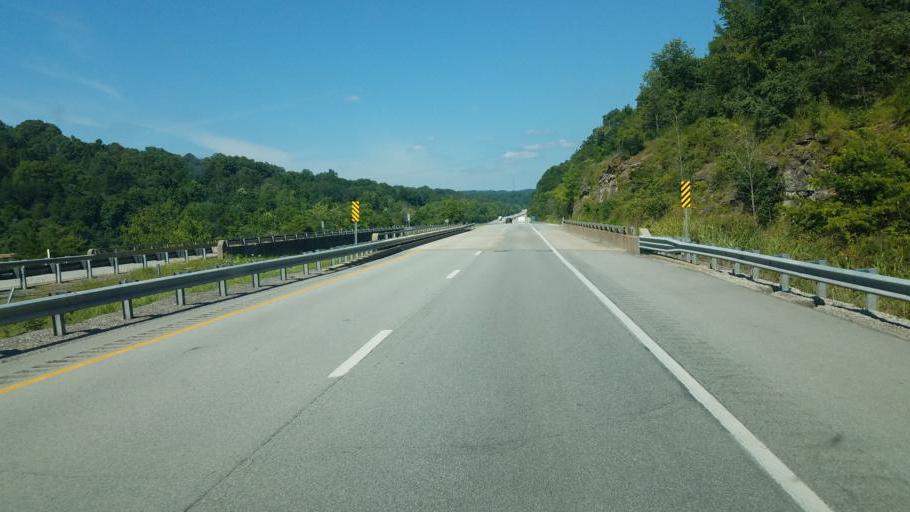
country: US
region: West Virginia
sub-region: Jackson County
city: Ravenswood
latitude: 38.8907
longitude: -81.7376
